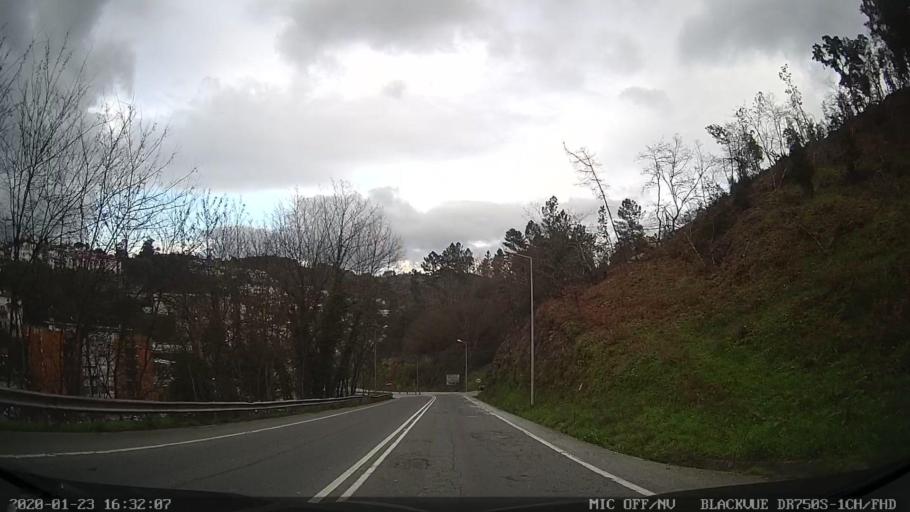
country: PT
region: Porto
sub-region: Amarante
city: Amarante
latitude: 41.2657
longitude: -8.0725
